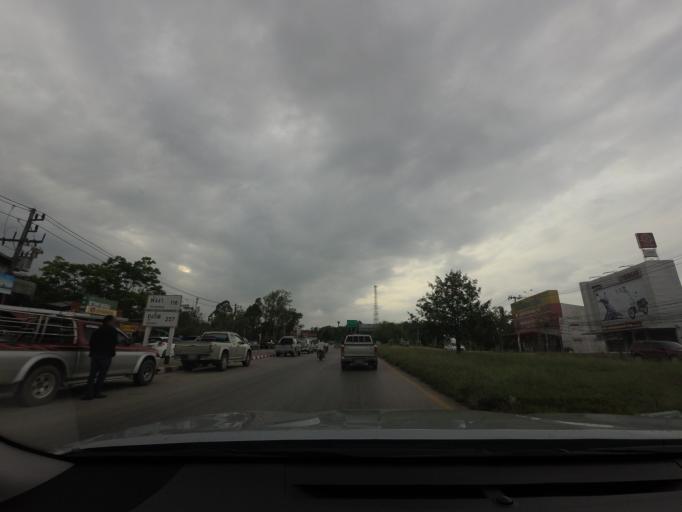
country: TH
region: Surat Thani
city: Phunphin
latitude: 9.0533
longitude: 99.1717
